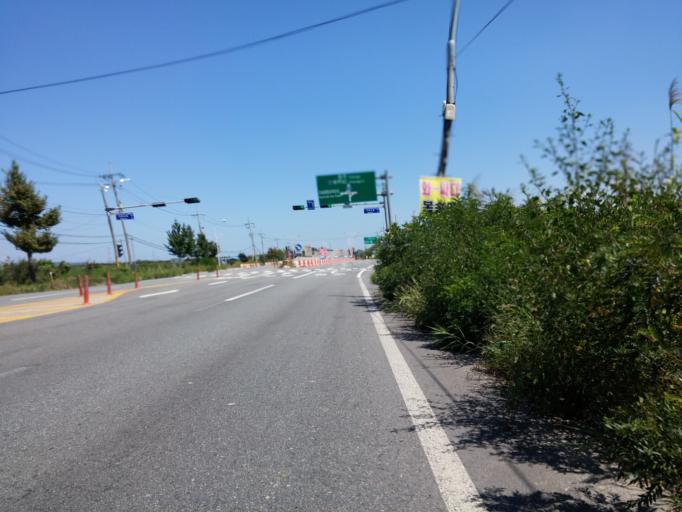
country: KR
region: Chungcheongbuk-do
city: Cheongju-si
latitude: 36.6164
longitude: 127.3368
